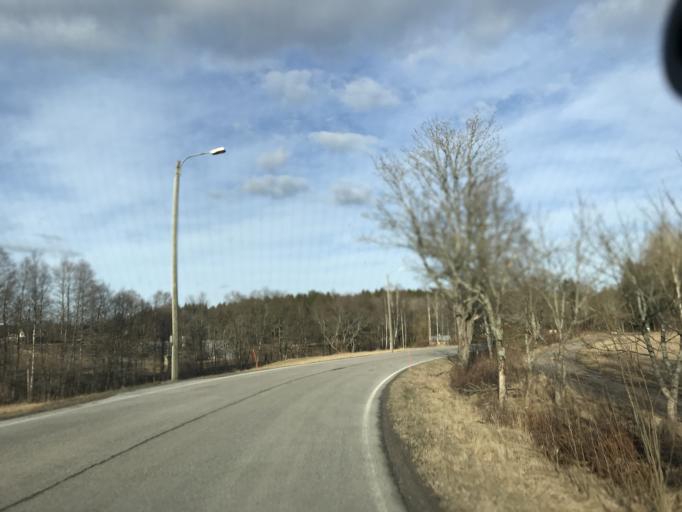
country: FI
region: Uusimaa
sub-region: Raaseporin
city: Ekenaes
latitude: 60.0870
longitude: 23.4122
